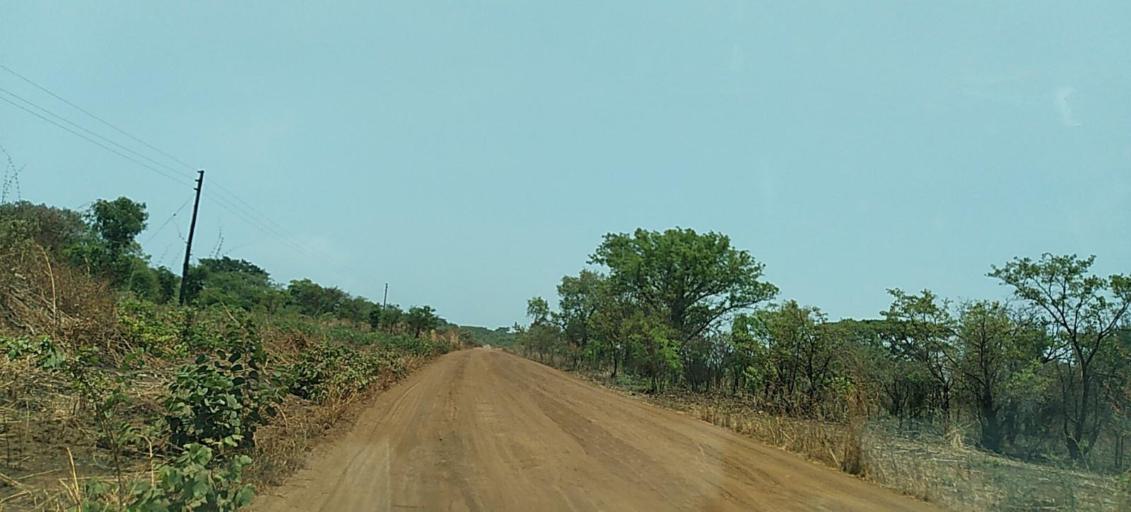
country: ZM
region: Copperbelt
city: Mpongwe
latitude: -13.6952
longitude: 27.8641
